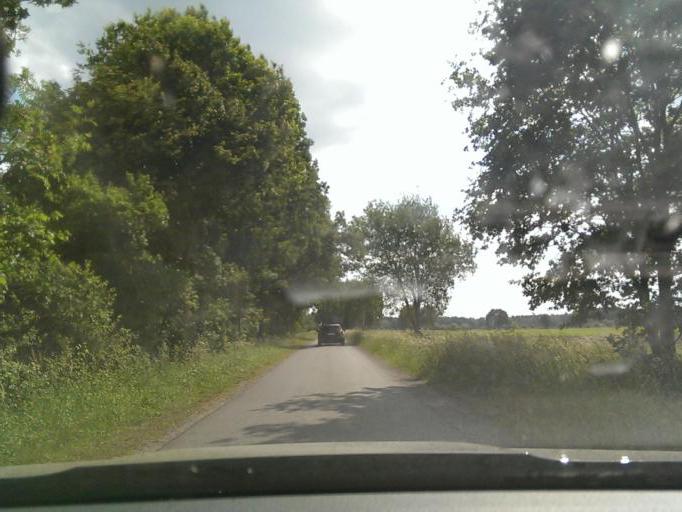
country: DE
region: Lower Saxony
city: Lindwedel
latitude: 52.5400
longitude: 9.6677
